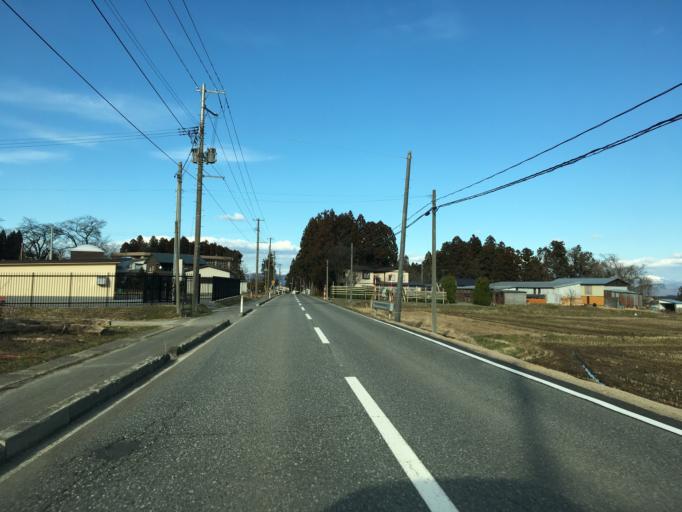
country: JP
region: Yamagata
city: Nagai
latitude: 38.0349
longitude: 139.9855
